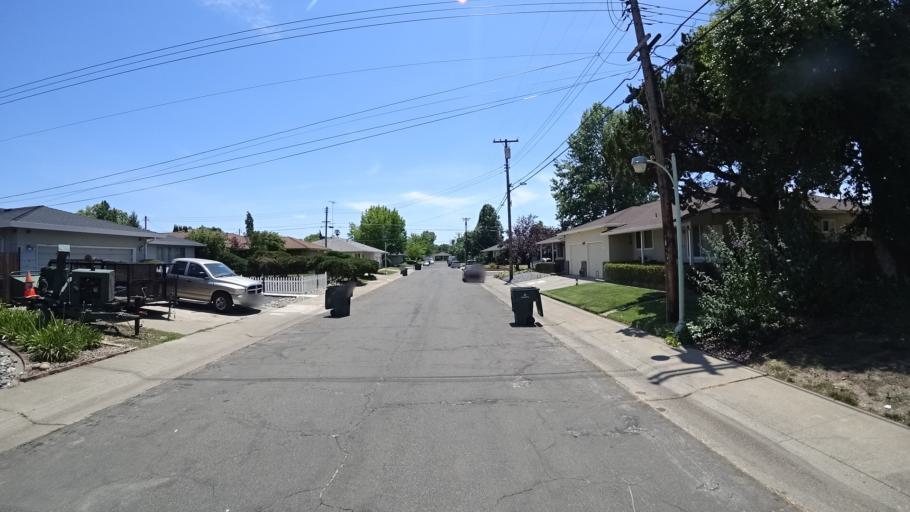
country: US
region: California
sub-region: Sacramento County
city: Florin
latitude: 38.5384
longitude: -121.4248
